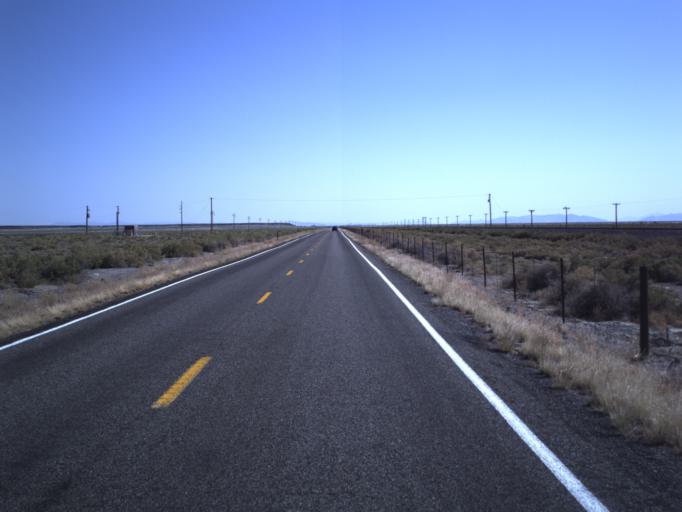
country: US
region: Utah
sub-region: Millard County
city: Delta
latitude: 39.1560
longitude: -112.7155
